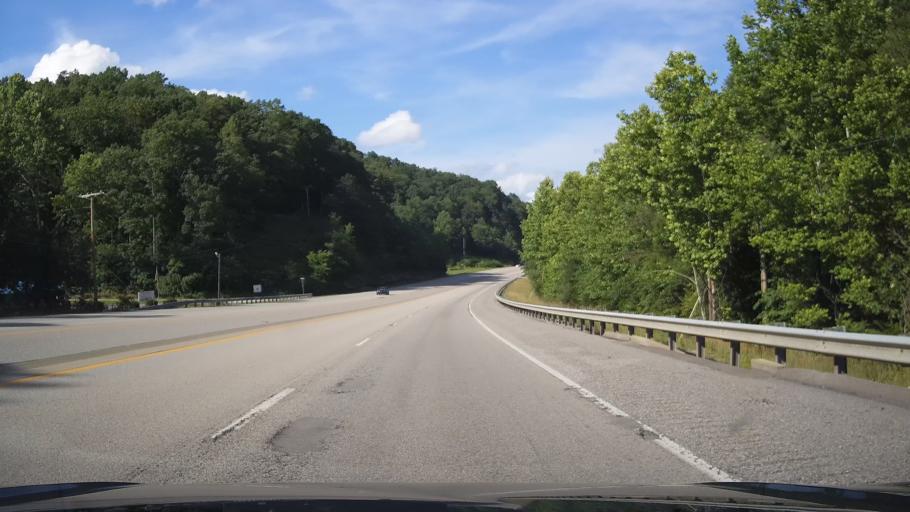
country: US
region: Kentucky
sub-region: Lawrence County
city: Louisa
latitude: 38.0479
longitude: -82.6437
